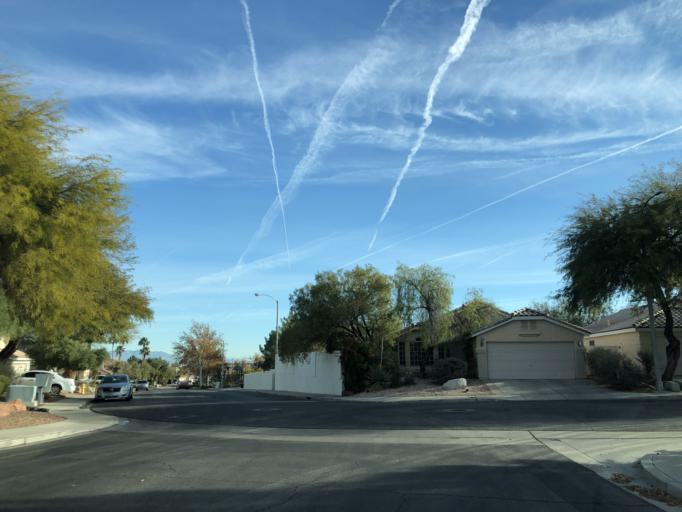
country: US
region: Nevada
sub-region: Clark County
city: Whitney
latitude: 36.0215
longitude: -115.0718
